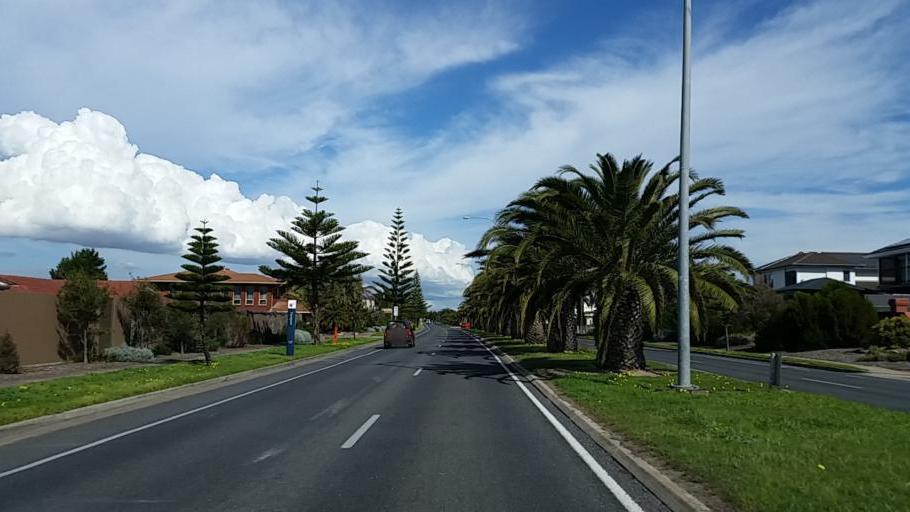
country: AU
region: South Australia
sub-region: Charles Sturt
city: Grange
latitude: -34.8823
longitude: 138.4856
